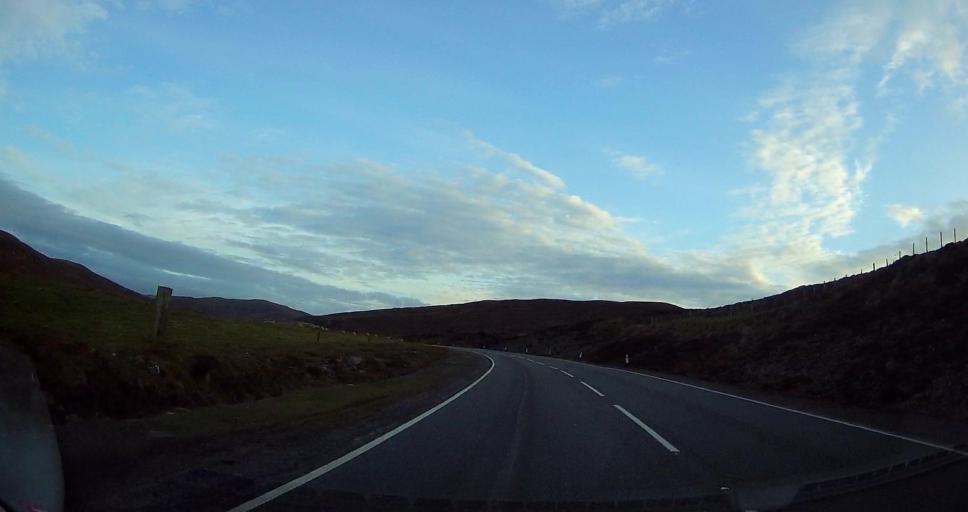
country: GB
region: Scotland
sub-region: Shetland Islands
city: Lerwick
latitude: 60.1587
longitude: -1.2316
